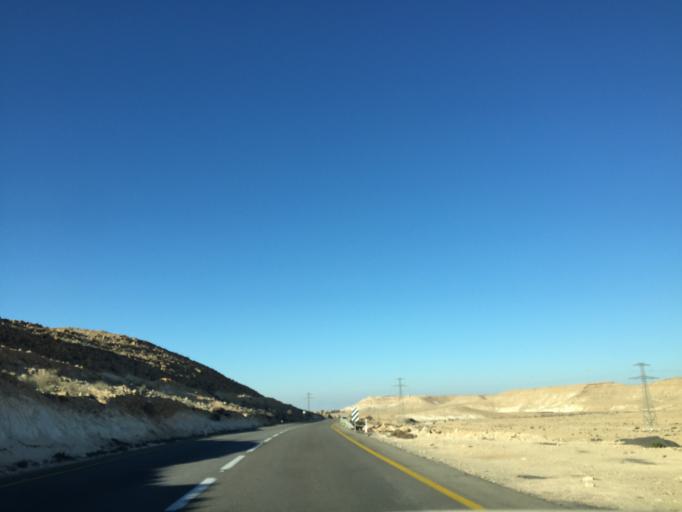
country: IL
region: Southern District
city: Midreshet Ben-Gurion
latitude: 30.7646
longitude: 34.7720
